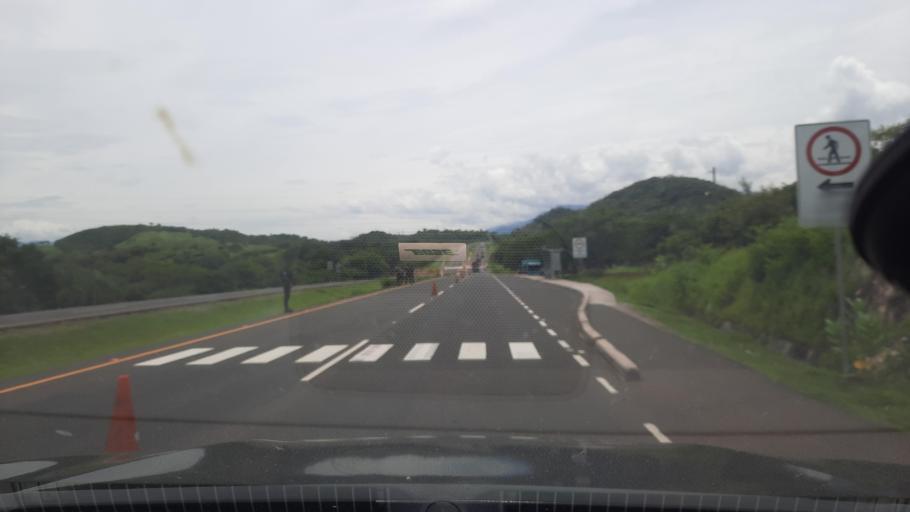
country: HN
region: Valle
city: Aramecina
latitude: 13.6726
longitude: -87.7329
